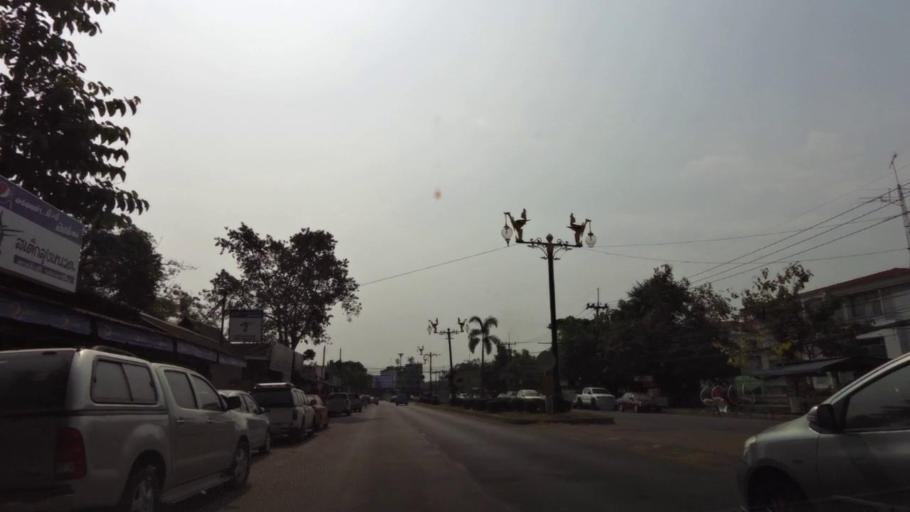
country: TH
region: Phra Nakhon Si Ayutthaya
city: Phra Nakhon Si Ayutthaya
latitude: 14.3464
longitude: 100.5645
